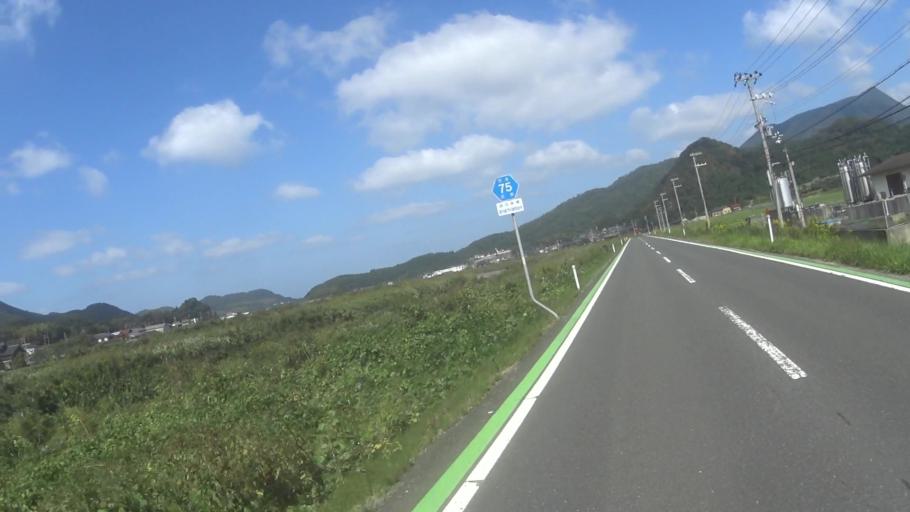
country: JP
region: Kyoto
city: Miyazu
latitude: 35.7148
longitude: 135.1064
